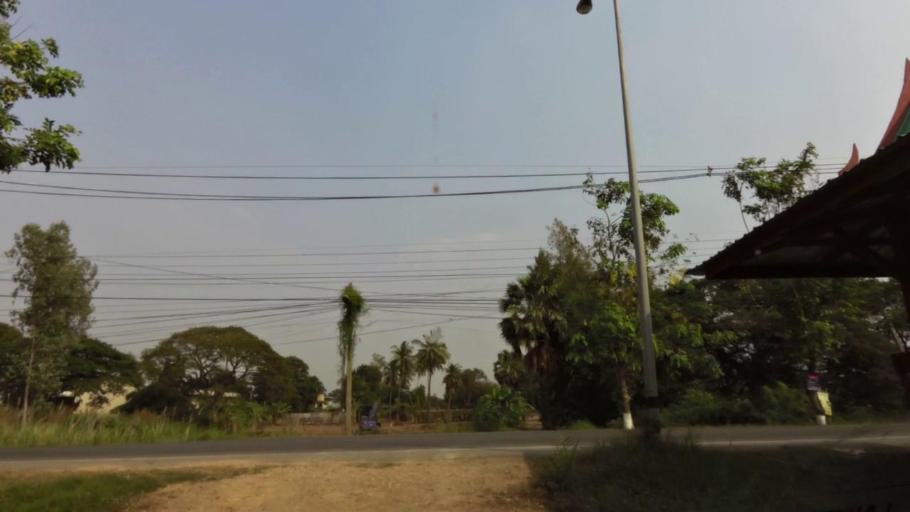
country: TH
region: Phra Nakhon Si Ayutthaya
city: Phra Nakhon Si Ayutthaya
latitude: 14.3389
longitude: 100.5746
